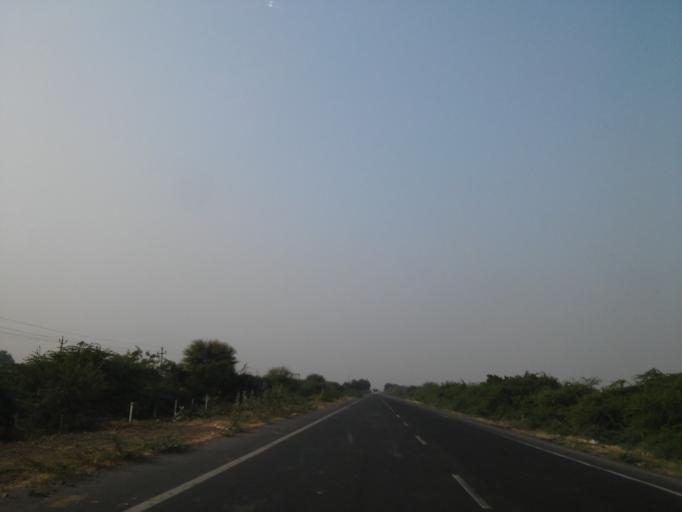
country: IN
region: Gujarat
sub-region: Kachchh
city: Anjar
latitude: 23.3060
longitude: 70.1114
